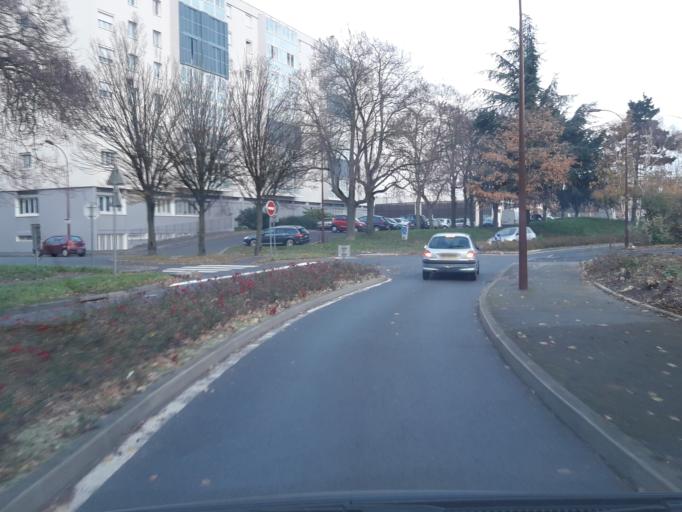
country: FR
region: Ile-de-France
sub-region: Departement de l'Essonne
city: Fleury-Merogis
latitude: 48.6405
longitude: 2.3484
